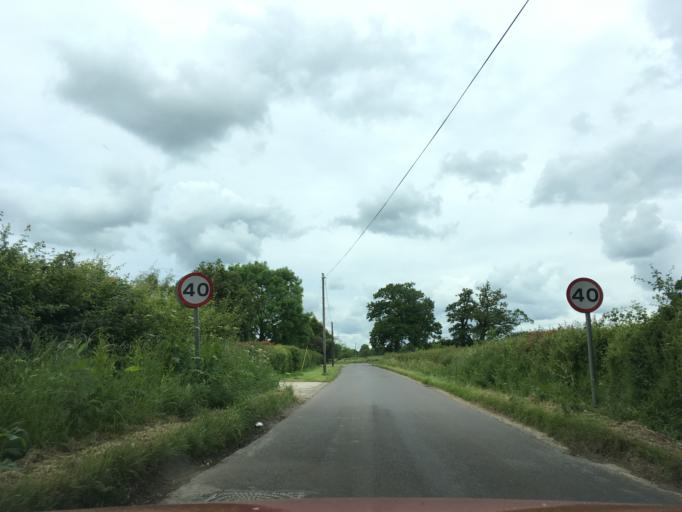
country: GB
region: England
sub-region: Wiltshire
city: Charlton
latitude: 51.5512
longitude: -2.0509
